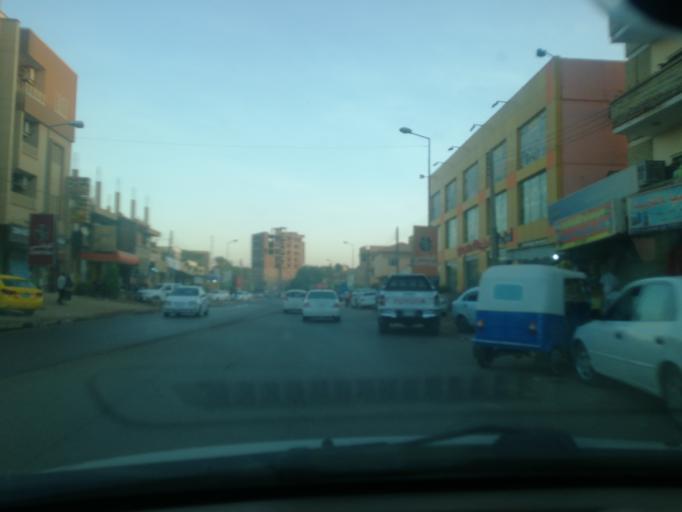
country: SD
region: Khartoum
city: Khartoum
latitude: 15.6229
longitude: 32.5575
